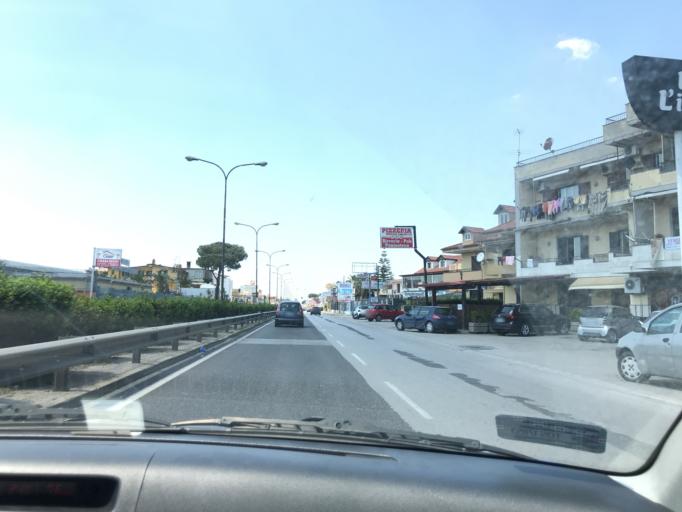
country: IT
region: Campania
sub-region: Provincia di Napoli
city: Villaricca
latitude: 40.9211
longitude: 14.1776
